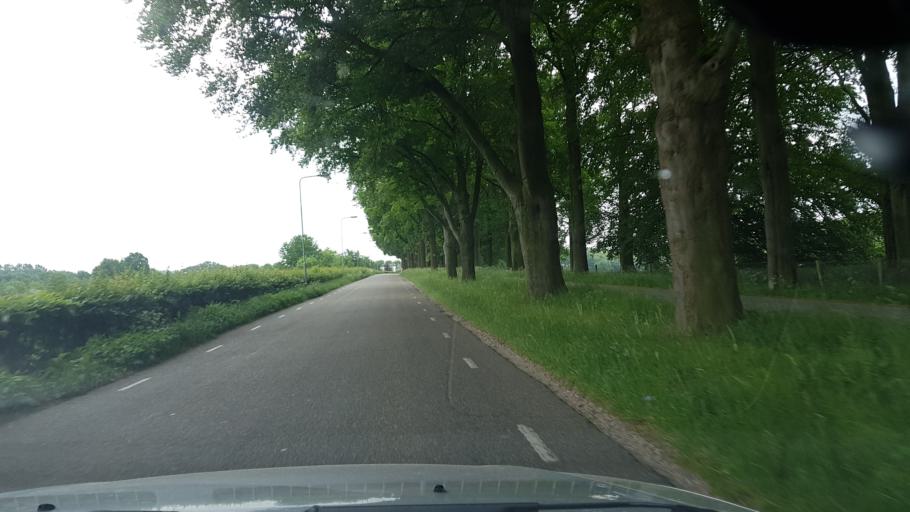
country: NL
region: Limburg
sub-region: Gemeente Stein
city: Stein
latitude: 50.9585
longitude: 5.7598
